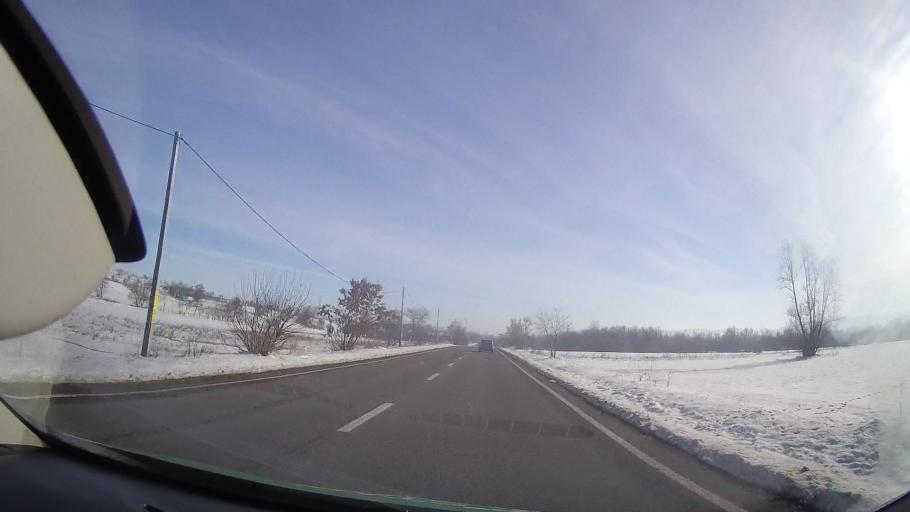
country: RO
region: Neamt
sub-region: Comuna Ghindaoani
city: Ghindaoani
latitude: 47.0768
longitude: 26.3521
